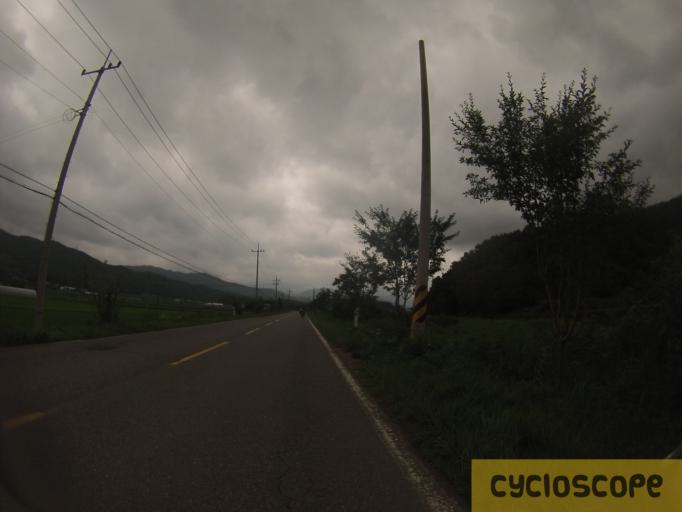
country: KR
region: Chungcheongnam-do
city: Yesan
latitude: 36.5729
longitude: 126.7849
